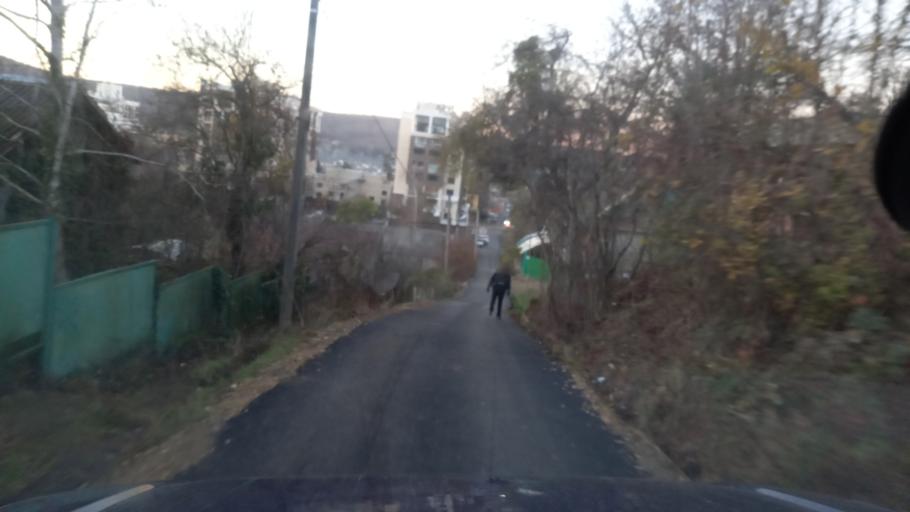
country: RU
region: Krasnodarskiy
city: Goryachiy Klyuch
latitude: 44.6238
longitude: 39.1038
